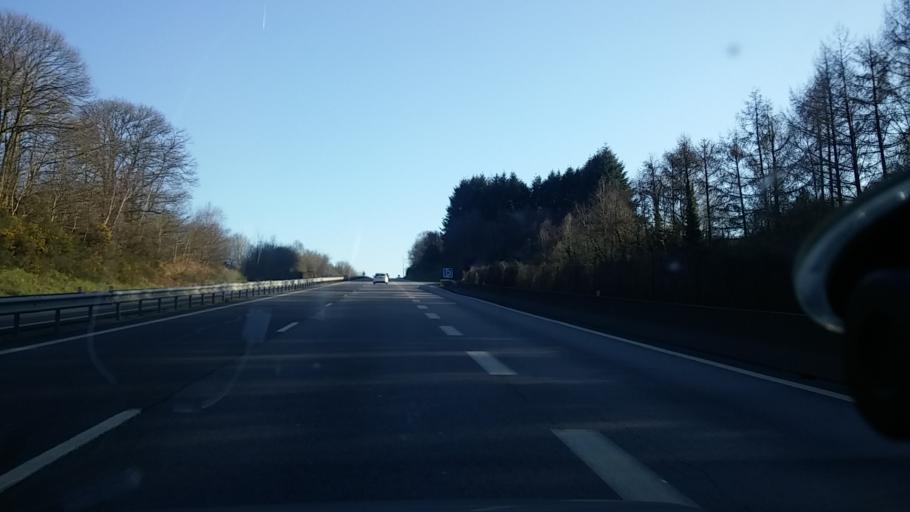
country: FR
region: Limousin
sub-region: Departement de la Haute-Vienne
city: Razes
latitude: 46.0651
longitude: 1.3610
